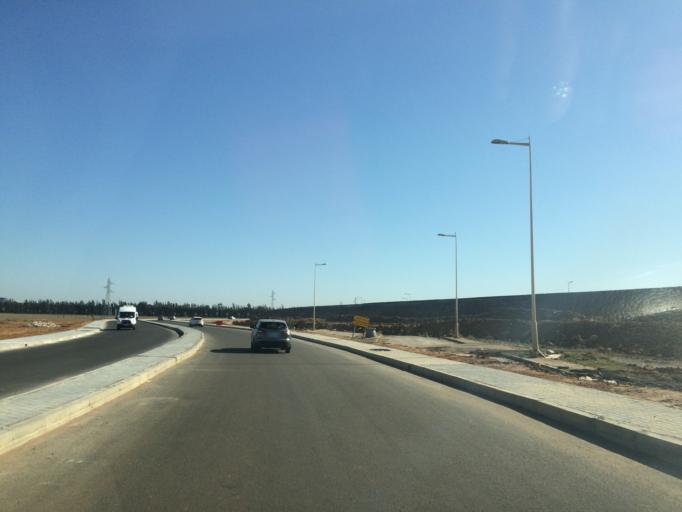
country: MA
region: Rabat-Sale-Zemmour-Zaer
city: Sale
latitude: 33.9841
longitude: -6.7310
